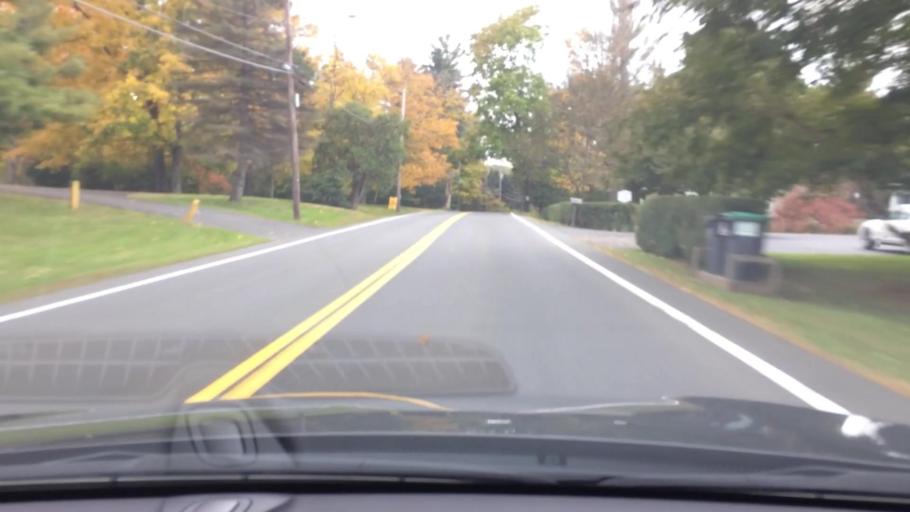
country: US
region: New York
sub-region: Columbia County
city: Lorenz Park
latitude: 42.2281
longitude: -73.7343
